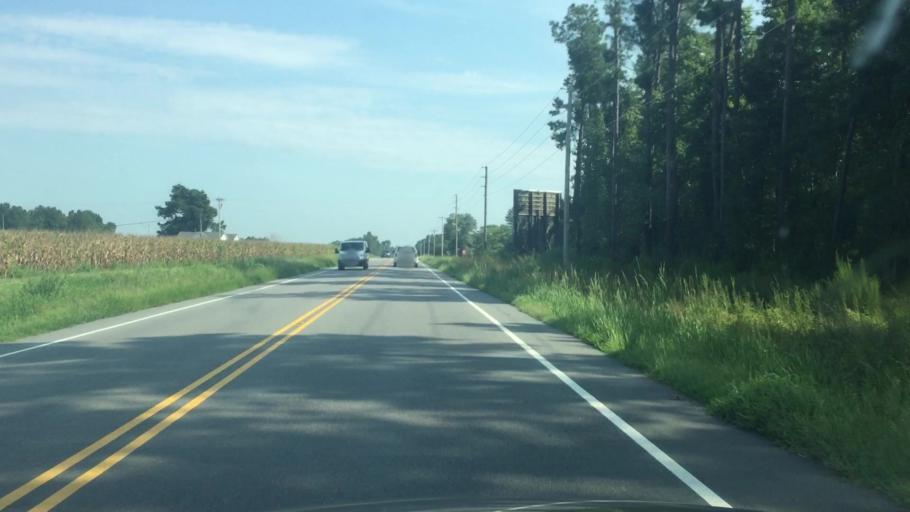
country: US
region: North Carolina
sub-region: Columbus County
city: Tabor City
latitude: 34.2176
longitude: -78.8239
